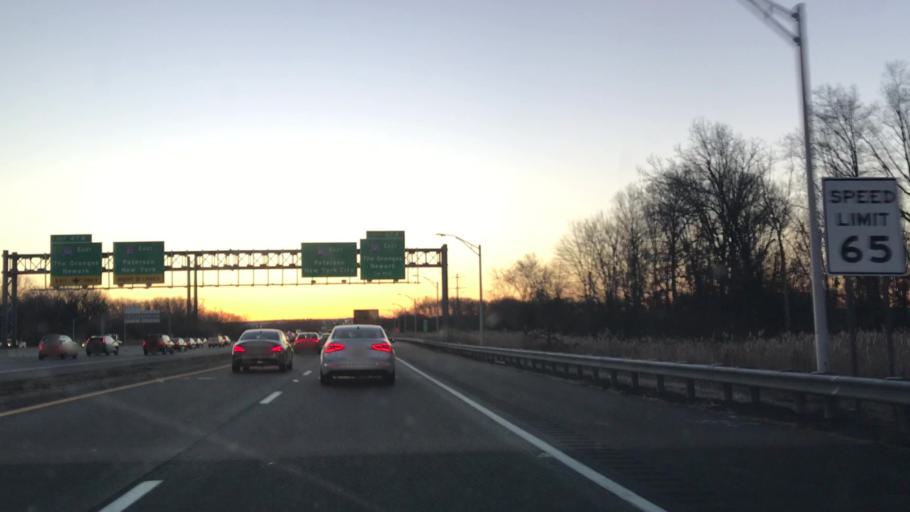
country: US
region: New Jersey
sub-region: Morris County
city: Parsippany
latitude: 40.8600
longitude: -74.3829
